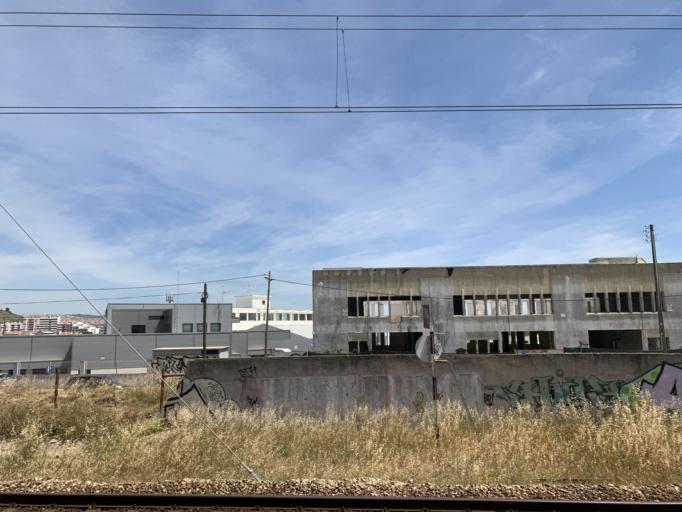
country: PT
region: Lisbon
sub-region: Amadora
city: Amadora
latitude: 38.7499
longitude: -9.2195
